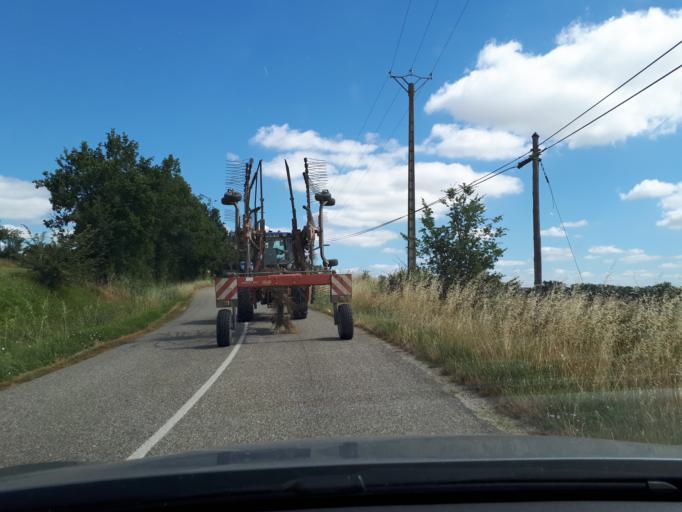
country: FR
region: Midi-Pyrenees
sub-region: Departement du Tarn-et-Garonne
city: Lavit
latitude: 43.9911
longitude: 0.8136
